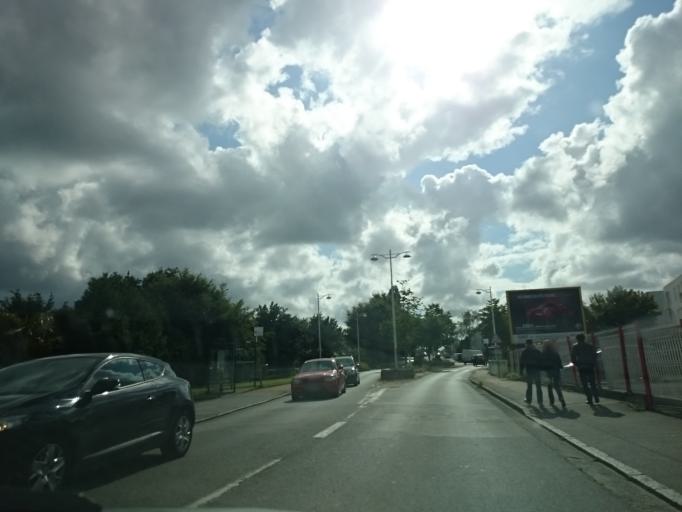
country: FR
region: Brittany
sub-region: Departement du Finistere
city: Brest
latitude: 48.4139
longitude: -4.4444
